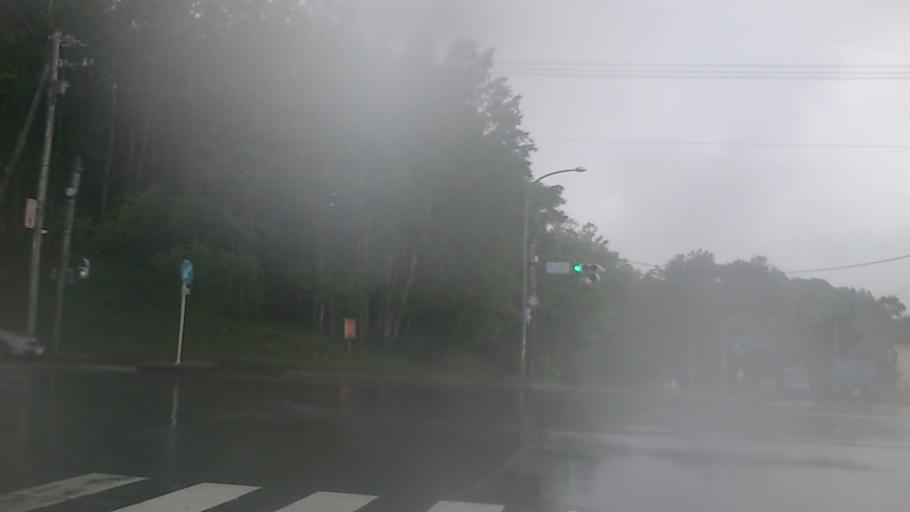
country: JP
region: Hokkaido
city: Obihiro
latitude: 42.9027
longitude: 143.1468
